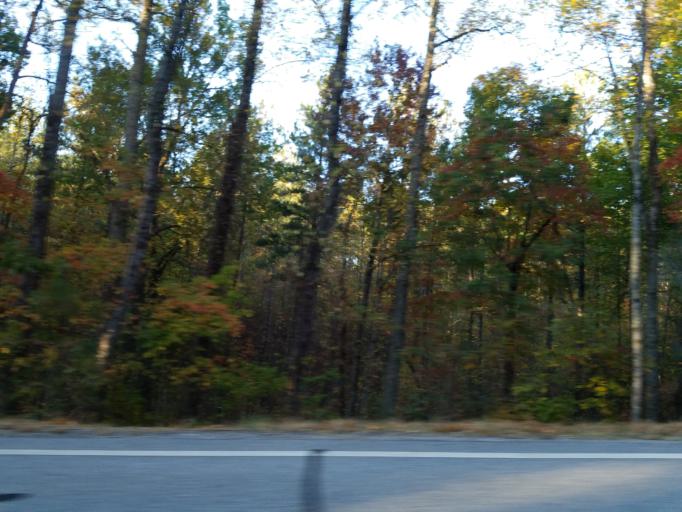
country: US
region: Georgia
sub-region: Dawson County
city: Dawsonville
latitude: 34.5489
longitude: -84.1459
